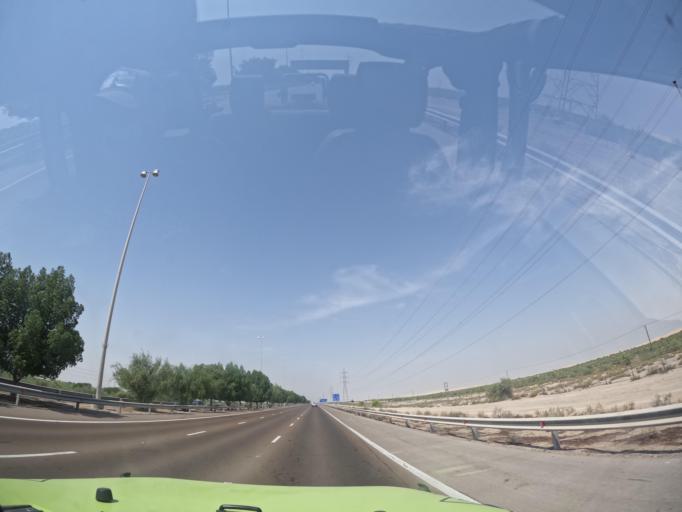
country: AE
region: Abu Dhabi
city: Abu Dhabi
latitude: 24.2163
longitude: 54.8735
